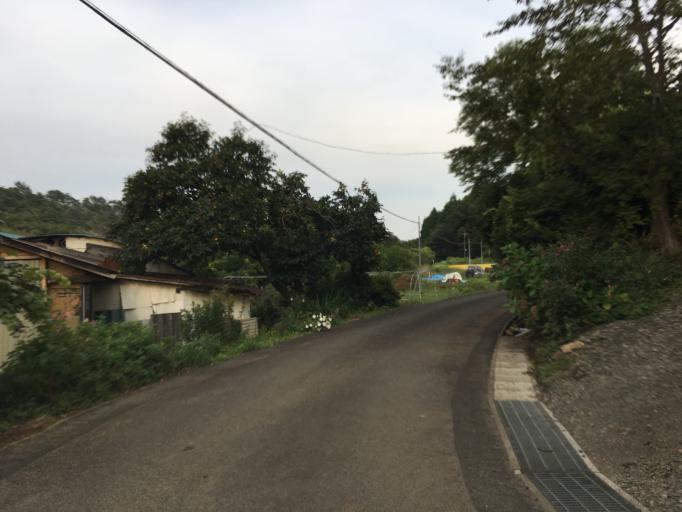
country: JP
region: Fukushima
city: Fukushima-shi
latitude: 37.7059
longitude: 140.3964
